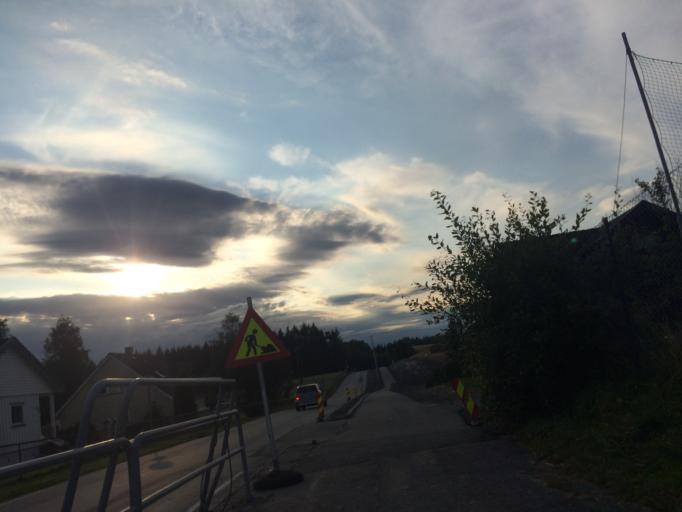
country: NO
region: Akershus
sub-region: Ski
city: Ski
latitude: 59.6832
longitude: 10.8770
